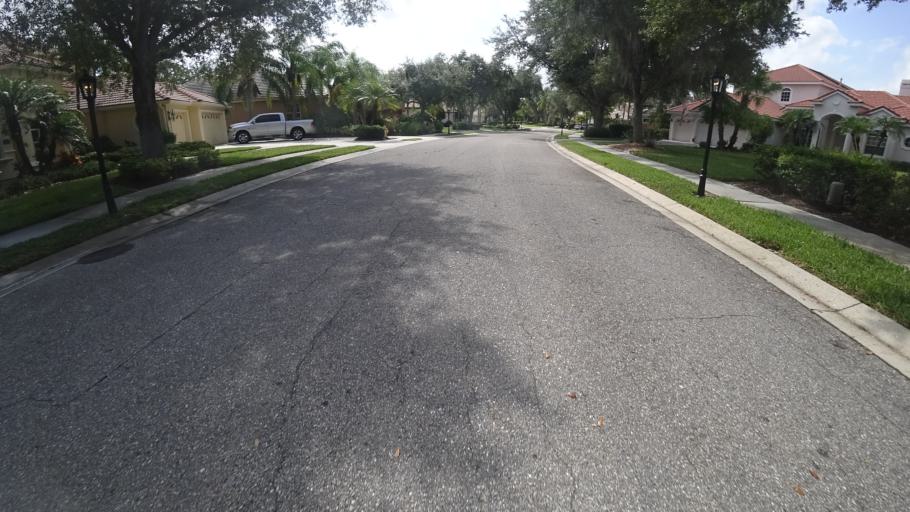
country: US
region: Florida
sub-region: Sarasota County
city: The Meadows
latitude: 27.3997
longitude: -82.4443
